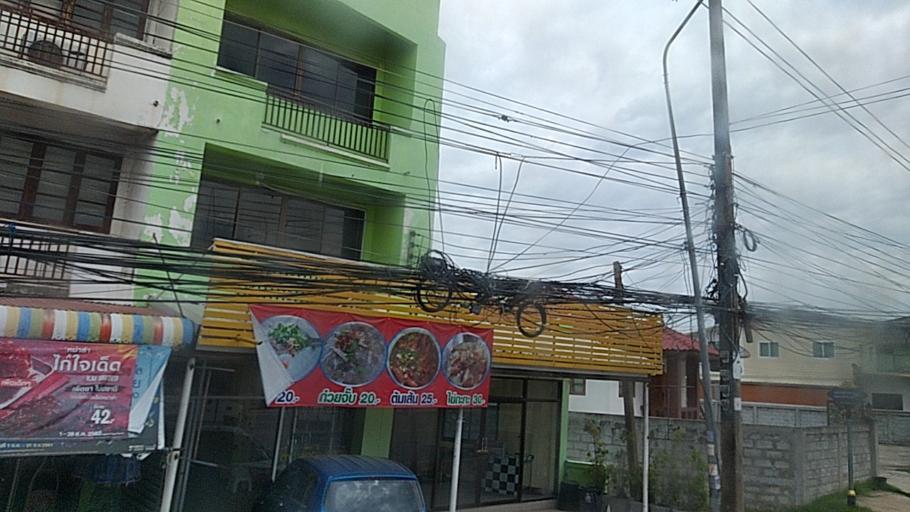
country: TH
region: Maha Sarakham
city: Maha Sarakham
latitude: 16.1725
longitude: 103.3188
